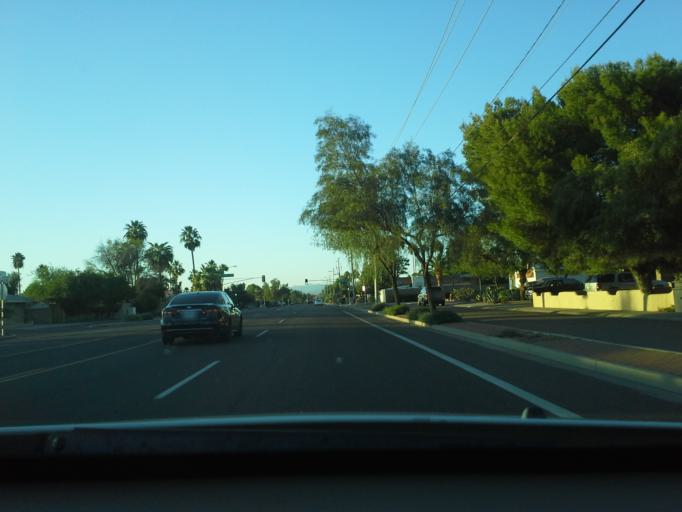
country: US
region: Arizona
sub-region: Maricopa County
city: Paradise Valley
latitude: 33.5887
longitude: -111.9957
